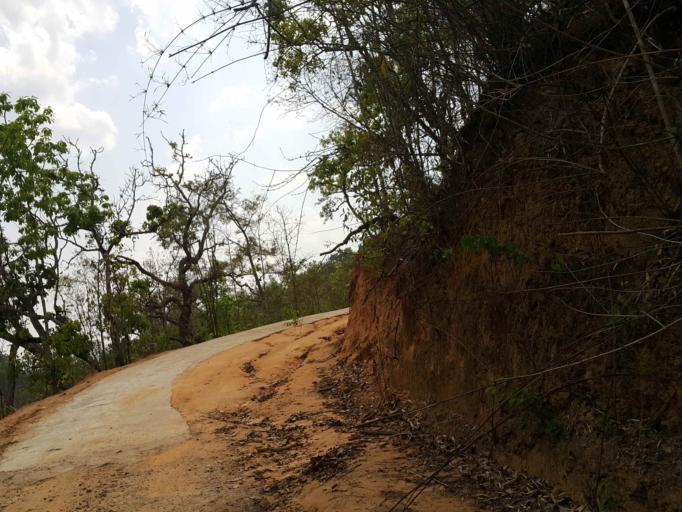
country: TH
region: Chiang Mai
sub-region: Amphoe Chiang Dao
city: Chiang Dao
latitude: 19.3070
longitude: 98.7336
